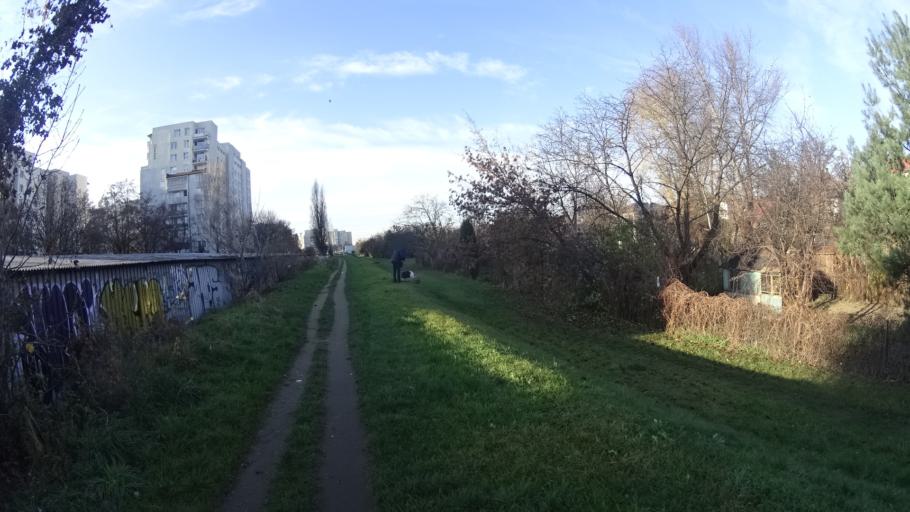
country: PL
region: Masovian Voivodeship
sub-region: Warszawa
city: Targowek
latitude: 52.2760
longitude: 21.0628
